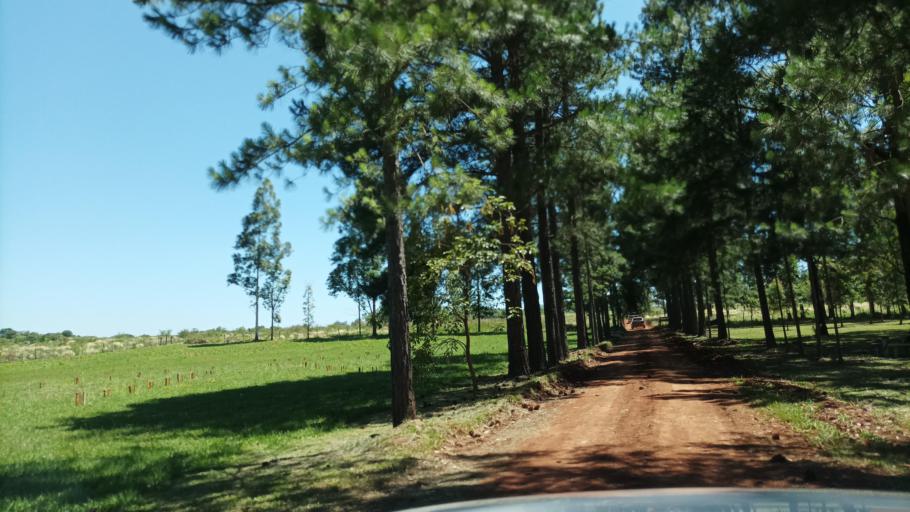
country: AR
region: Misiones
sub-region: Departamento de Apostoles
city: San Jose
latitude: -27.7863
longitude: -55.7036
